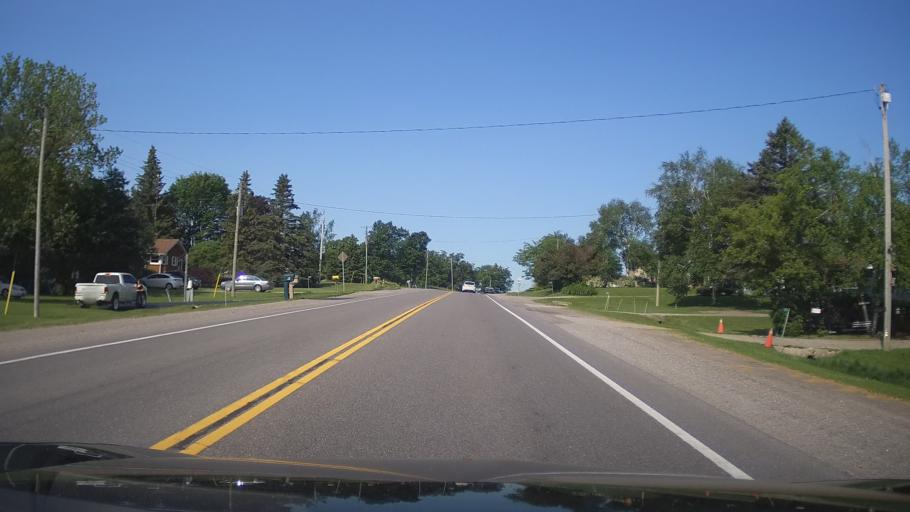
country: CA
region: Ontario
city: Omemee
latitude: 44.3472
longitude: -78.8097
